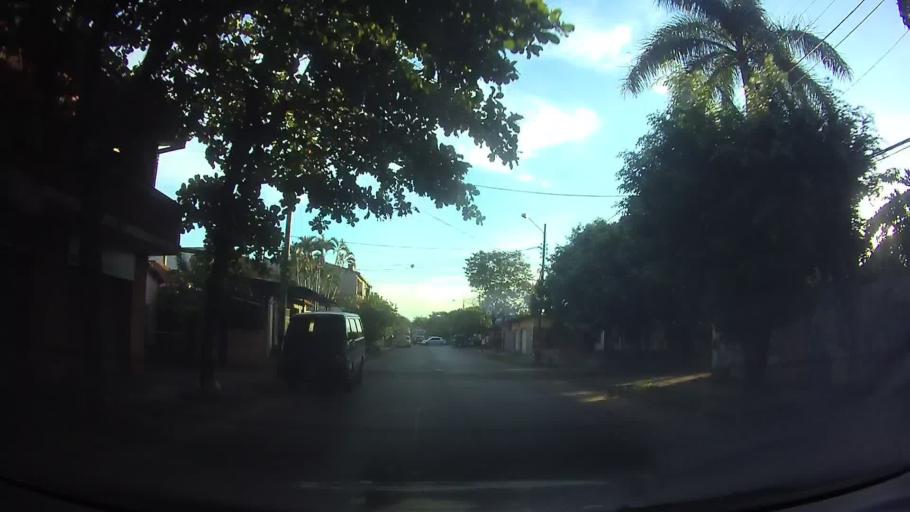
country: PY
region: Central
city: San Lorenzo
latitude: -25.2695
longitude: -57.4972
